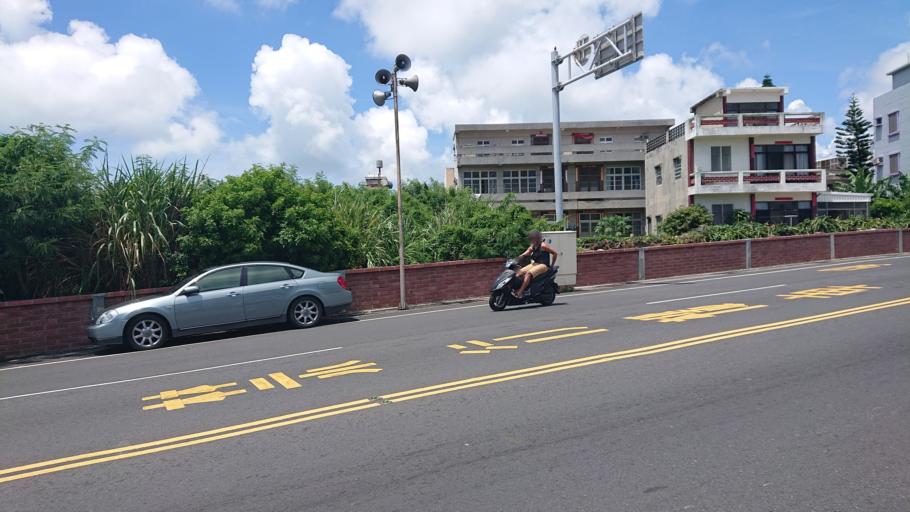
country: TW
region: Taiwan
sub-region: Penghu
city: Ma-kung
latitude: 23.5691
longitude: 119.5997
